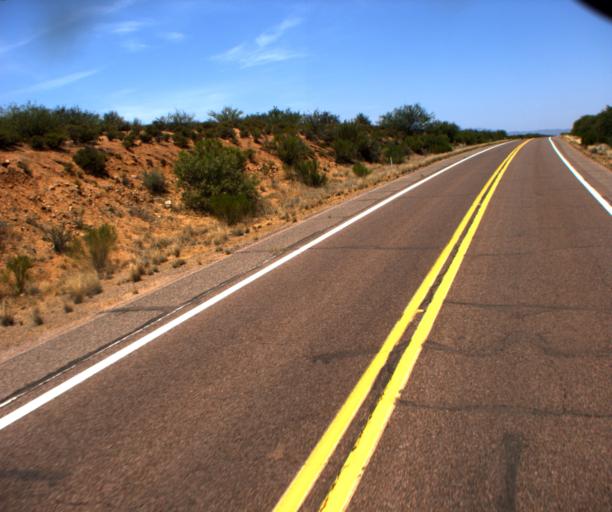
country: US
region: Arizona
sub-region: Gila County
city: Tonto Basin
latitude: 33.7913
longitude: -111.2669
